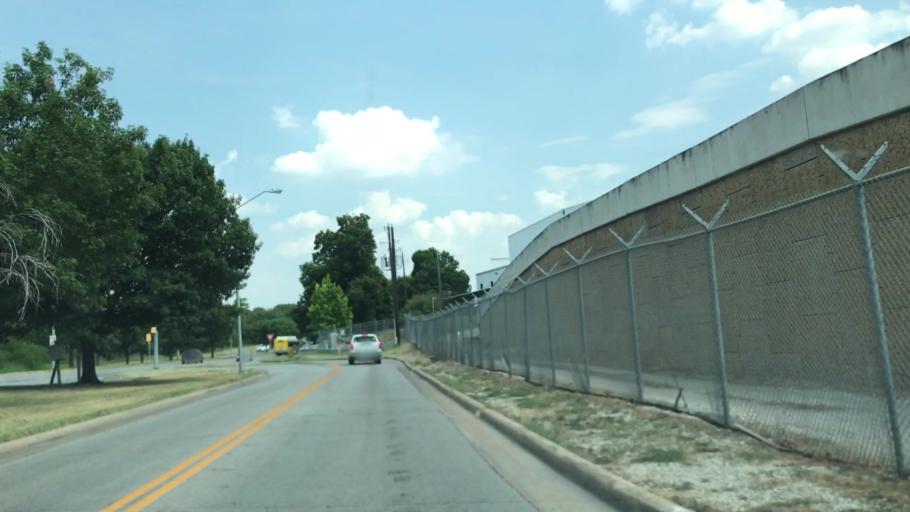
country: US
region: Texas
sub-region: Dallas County
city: University Park
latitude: 32.8590
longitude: -96.8517
